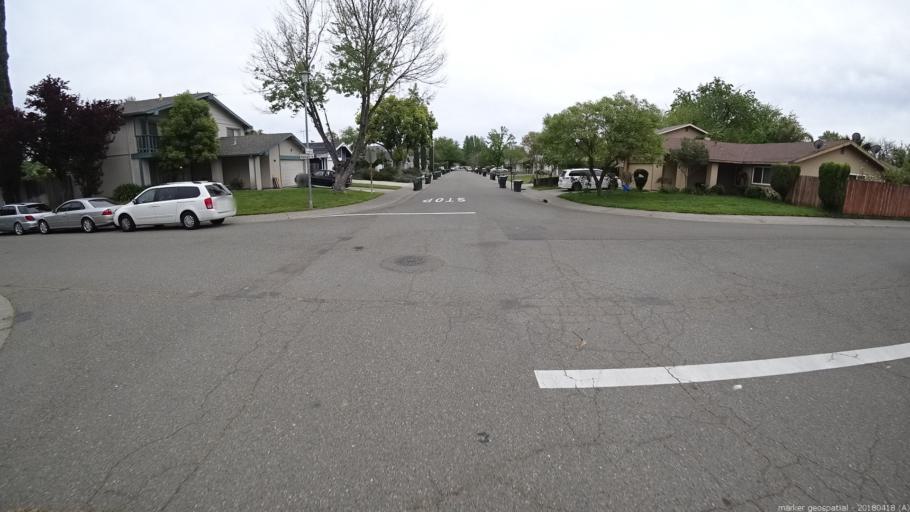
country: US
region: California
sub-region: Sacramento County
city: La Riviera
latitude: 38.5731
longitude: -121.3479
